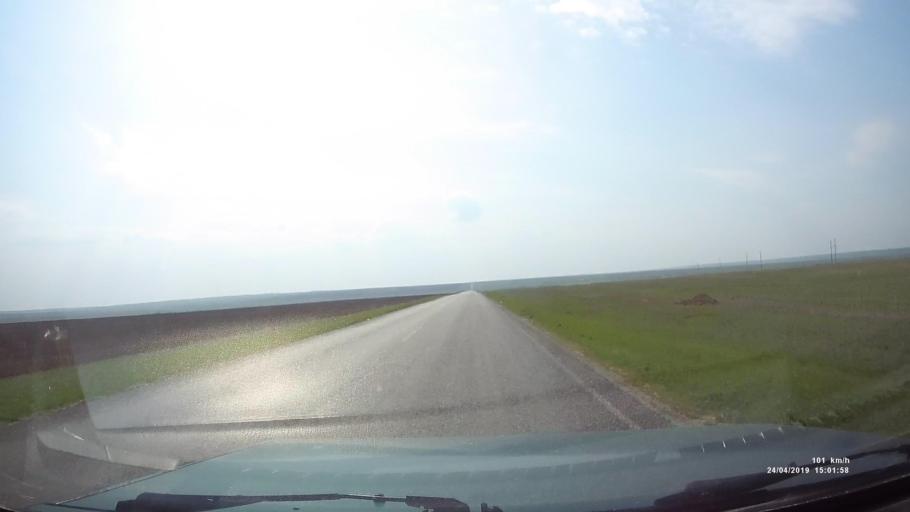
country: RU
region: Rostov
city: Remontnoye
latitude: 46.5667
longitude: 43.5222
